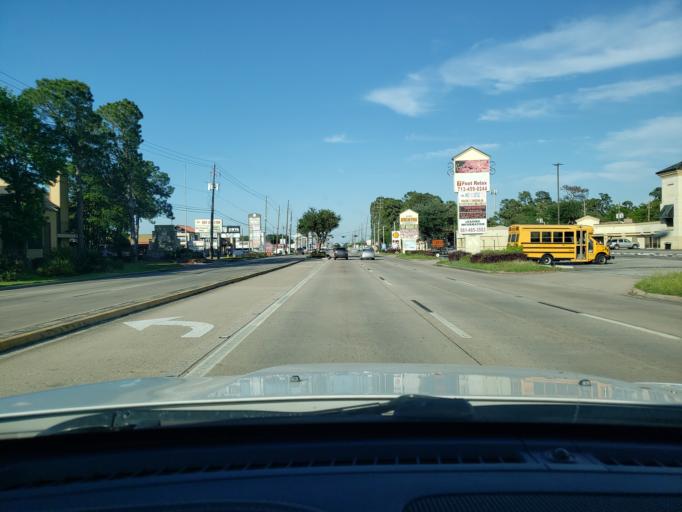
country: US
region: Texas
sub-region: Harris County
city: Hudson
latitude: 29.9822
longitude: -95.5087
